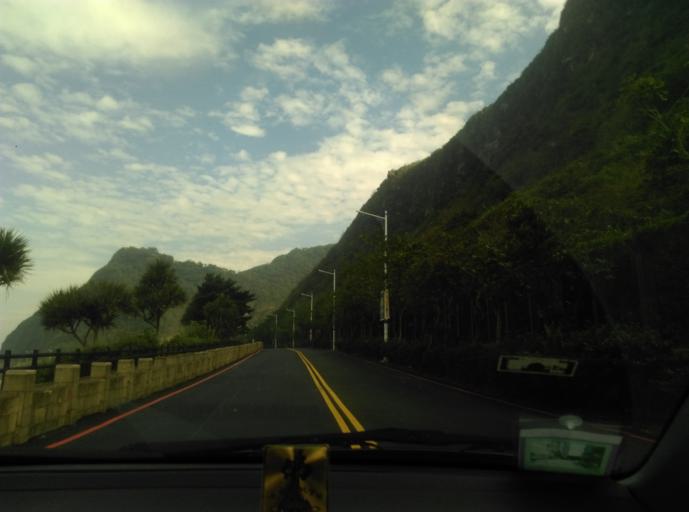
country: TW
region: Taiwan
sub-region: Keelung
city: Keelung
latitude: 25.1640
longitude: 121.7086
